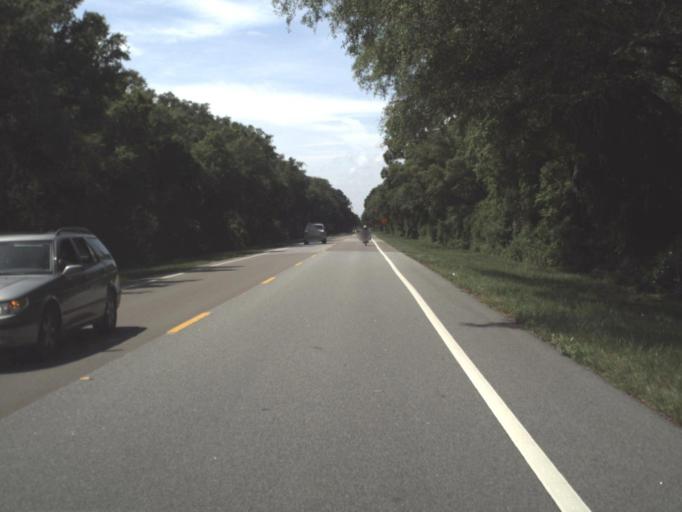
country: US
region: Florida
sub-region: Nassau County
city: Fernandina Beach
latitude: 30.4990
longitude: -81.4489
